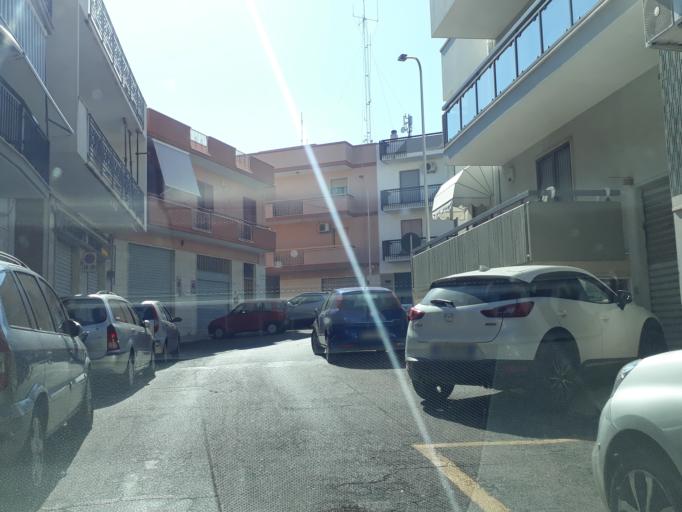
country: IT
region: Apulia
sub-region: Provincia di Bari
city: Monopoli
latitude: 40.9492
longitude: 17.2948
